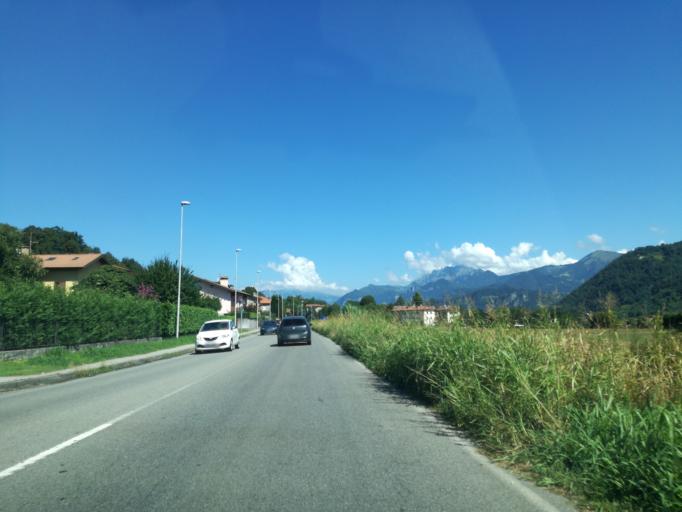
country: IT
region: Lombardy
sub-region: Provincia di Lecco
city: Imbersago
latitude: 45.7075
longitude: 9.4493
